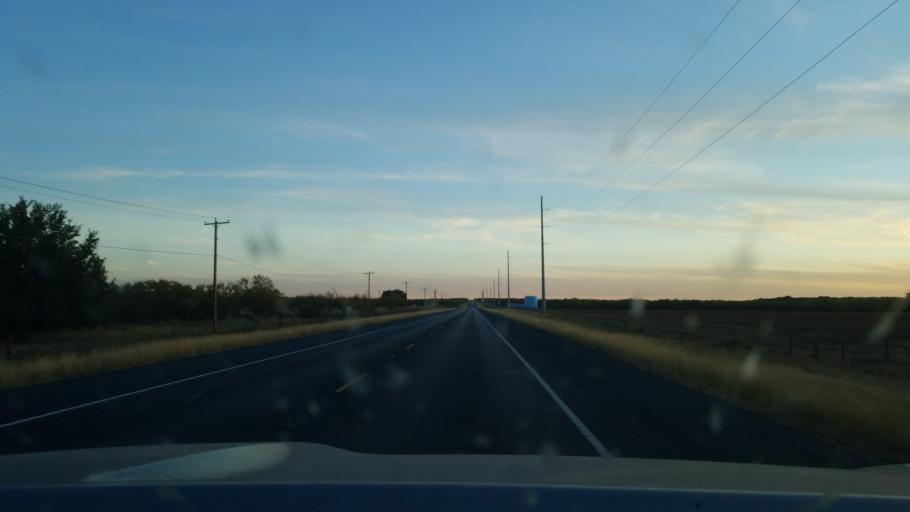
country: US
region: Texas
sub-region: Stephens County
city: Breckenridge
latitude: 32.7123
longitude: -98.9025
